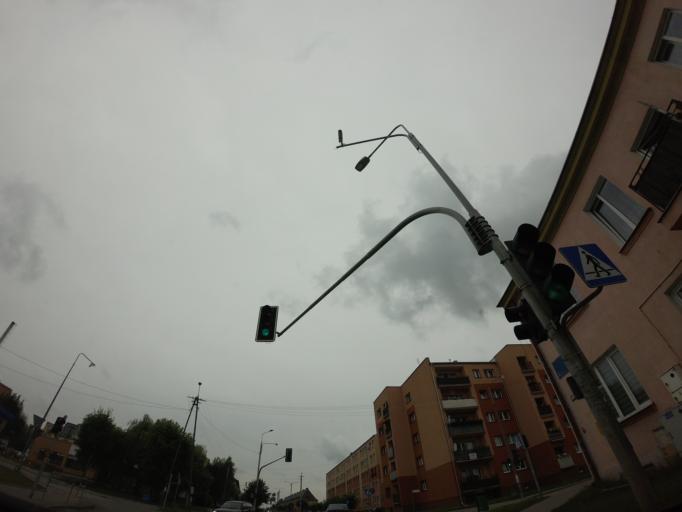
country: PL
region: Masovian Voivodeship
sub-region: Powiat makowski
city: Makow Mazowiecki
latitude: 52.8653
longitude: 21.0984
